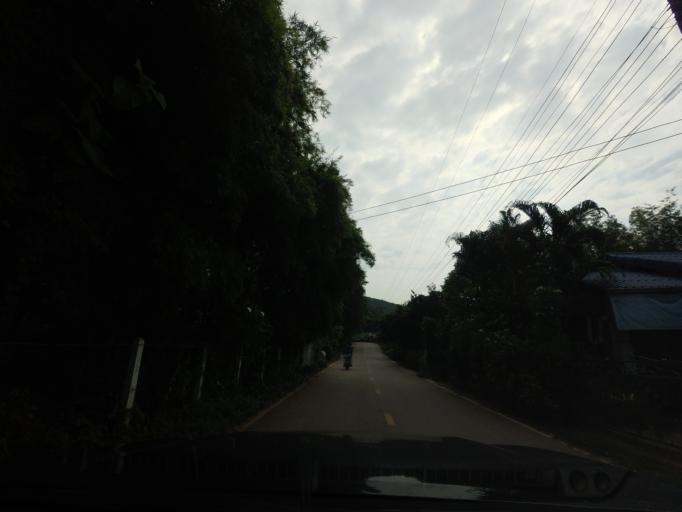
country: TH
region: Loei
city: Chiang Khan
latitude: 17.8104
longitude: 101.5600
